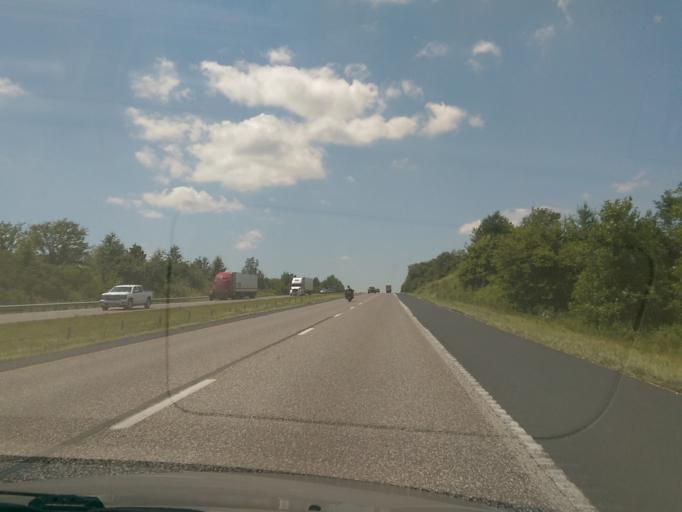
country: US
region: Missouri
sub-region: Cooper County
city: Boonville
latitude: 38.9384
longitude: -92.6596
